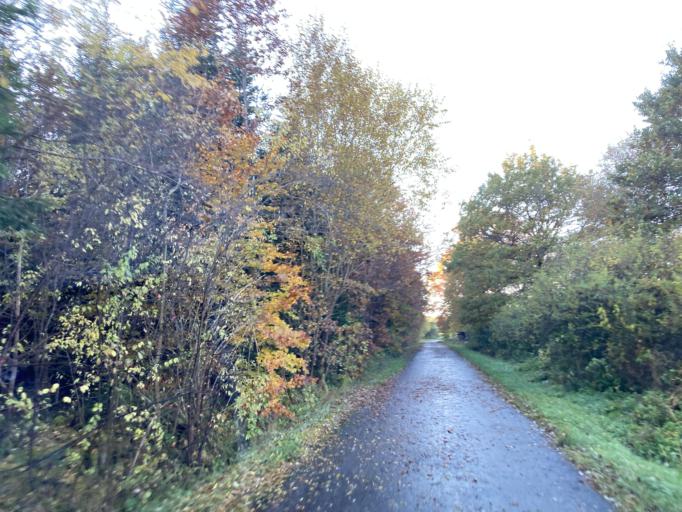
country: DE
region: Baden-Wuerttemberg
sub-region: Tuebingen Region
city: Bodelshausen
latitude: 48.4299
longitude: 8.9519
